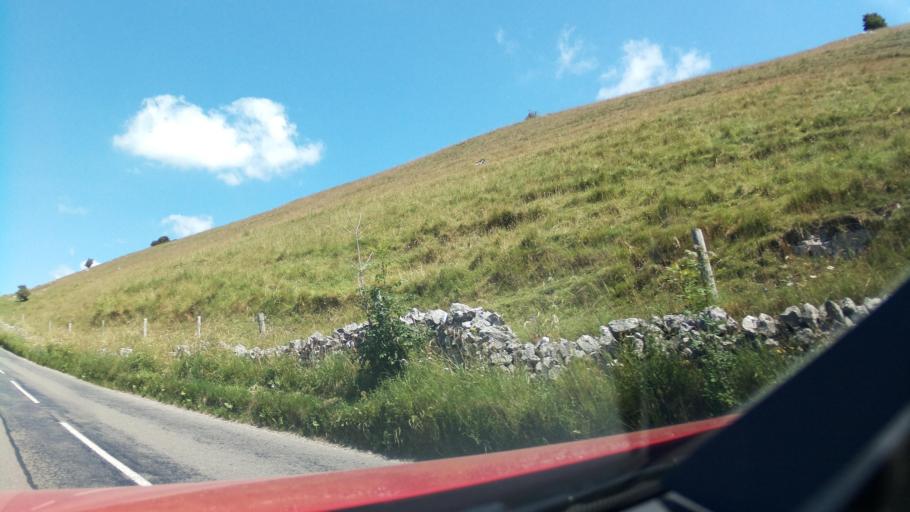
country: GB
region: England
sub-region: Derbyshire
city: Buxton
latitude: 53.2087
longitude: -1.8705
